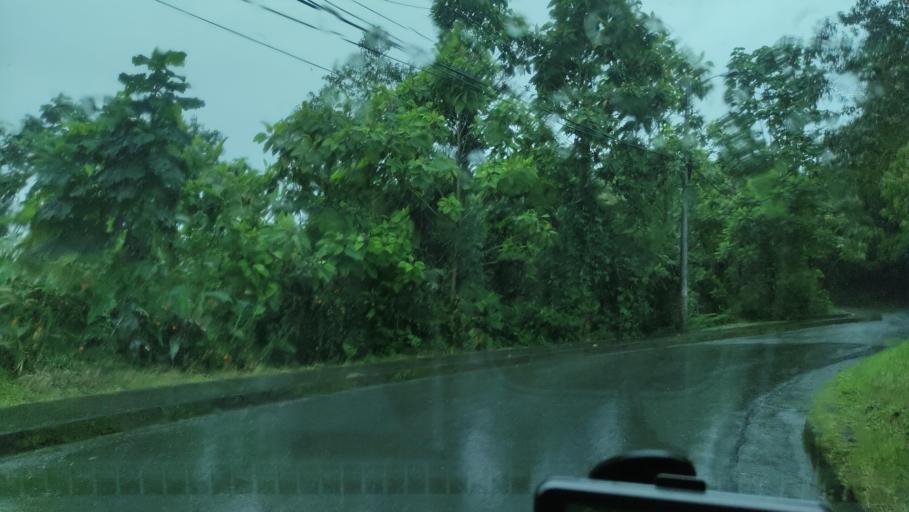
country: CO
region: Caldas
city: Villamaria
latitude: 5.0527
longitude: -75.4768
